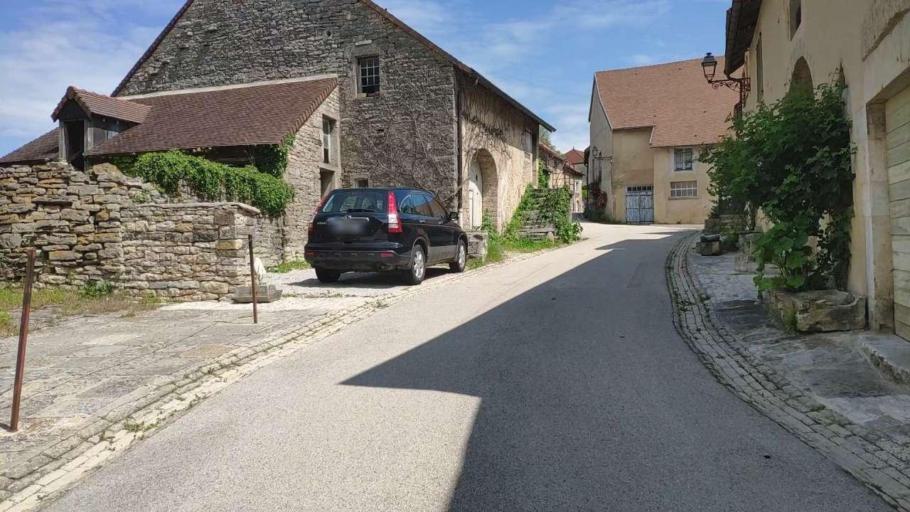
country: FR
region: Franche-Comte
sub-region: Departement du Jura
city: Perrigny
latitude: 46.7548
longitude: 5.6238
